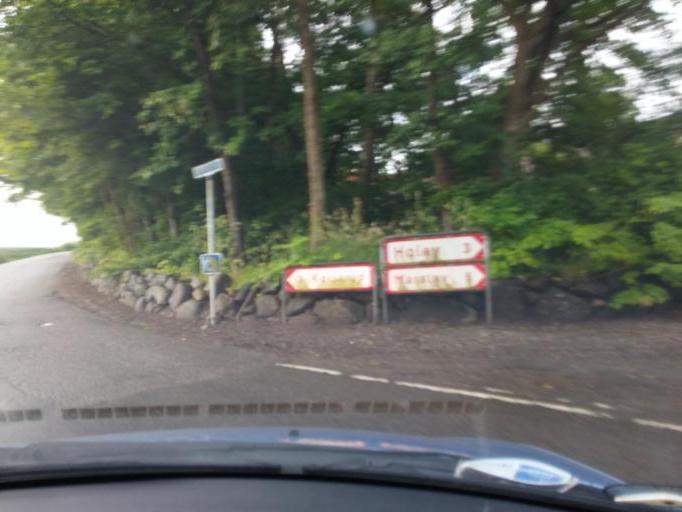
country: DK
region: South Denmark
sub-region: Kerteminde Kommune
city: Munkebo
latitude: 55.4273
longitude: 10.5383
